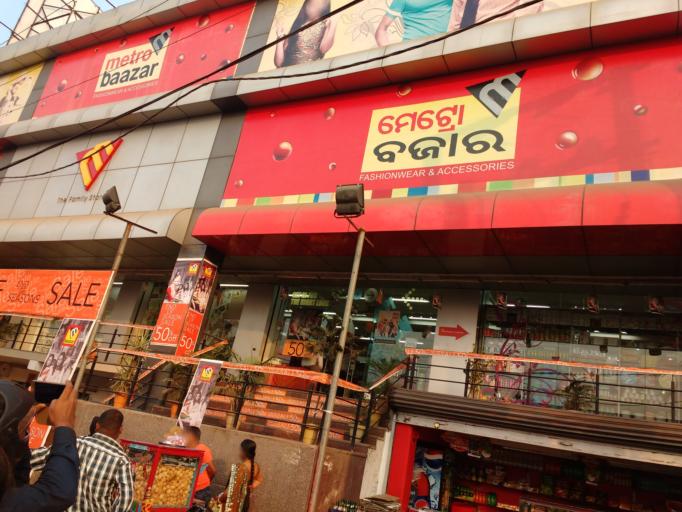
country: IN
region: Odisha
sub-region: Cuttack
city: Cuttack
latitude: 20.4613
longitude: 85.8823
